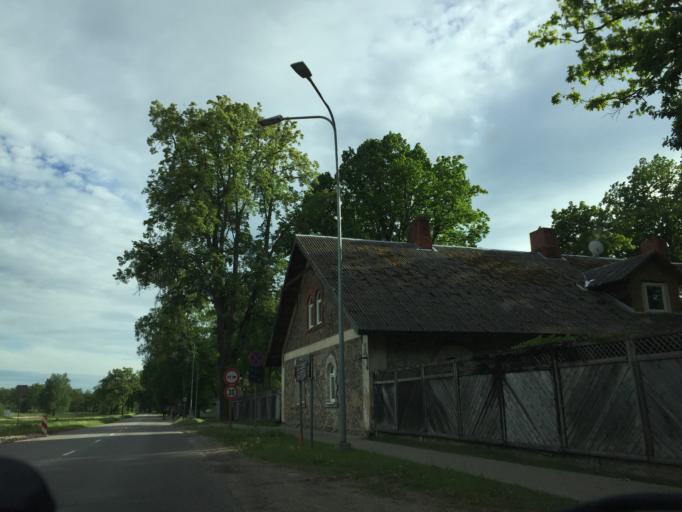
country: LV
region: Valmieras Rajons
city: Valmiera
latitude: 57.5226
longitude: 25.4202
